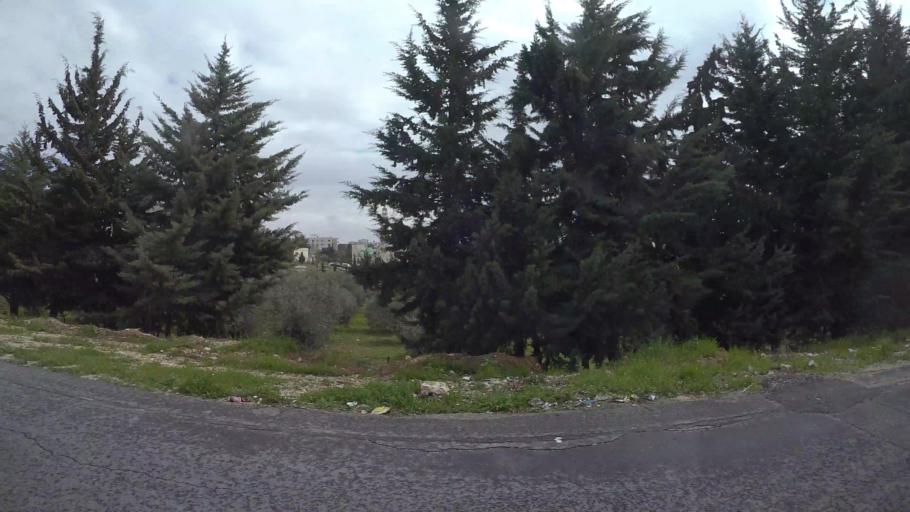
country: JO
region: Amman
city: Al Jubayhah
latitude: 31.9933
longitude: 35.8546
